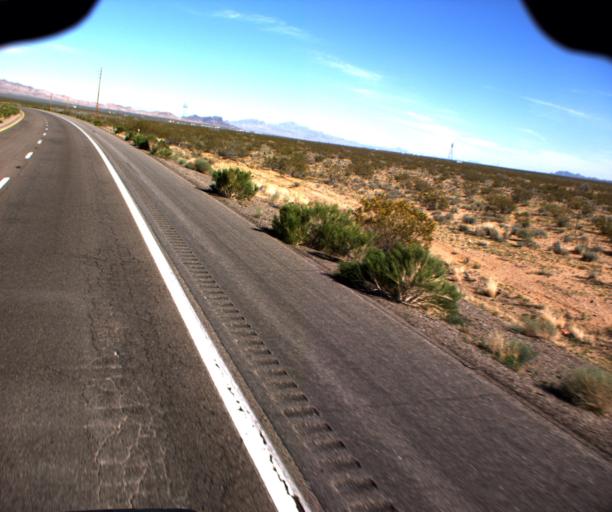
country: US
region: Arizona
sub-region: Mohave County
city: Dolan Springs
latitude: 35.6617
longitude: -114.4500
